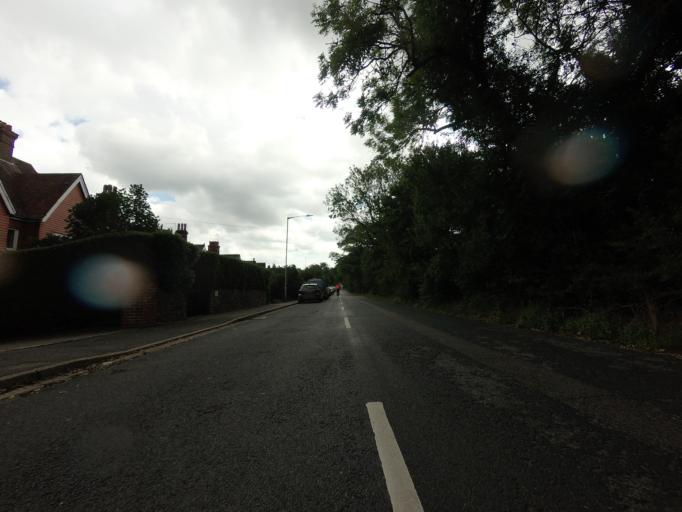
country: GB
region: England
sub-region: Kent
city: Shoreham
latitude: 51.3040
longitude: 0.1597
